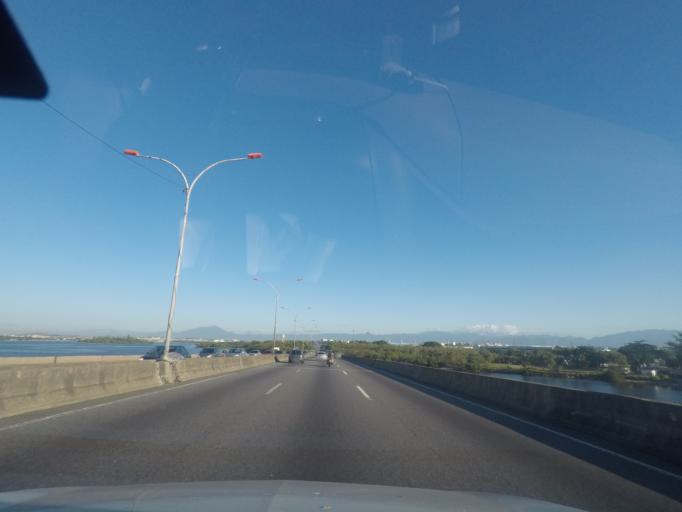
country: BR
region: Rio de Janeiro
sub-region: Rio De Janeiro
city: Rio de Janeiro
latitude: -22.8340
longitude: -43.2449
